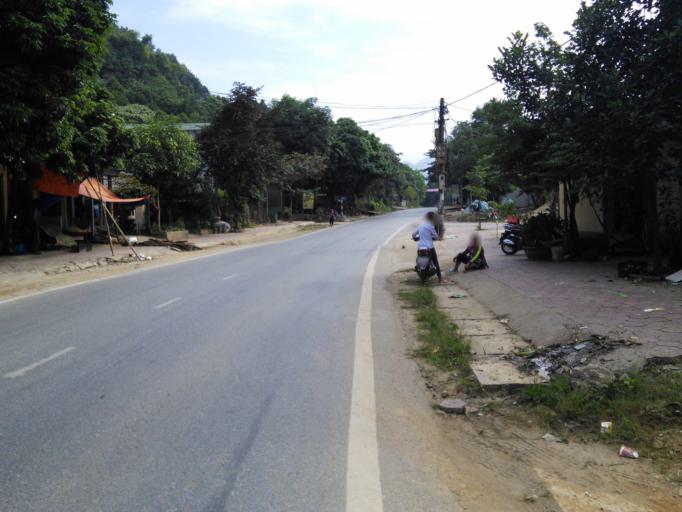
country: VN
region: Lao Cai
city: Lao Cai
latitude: 22.4637
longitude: 103.9473
